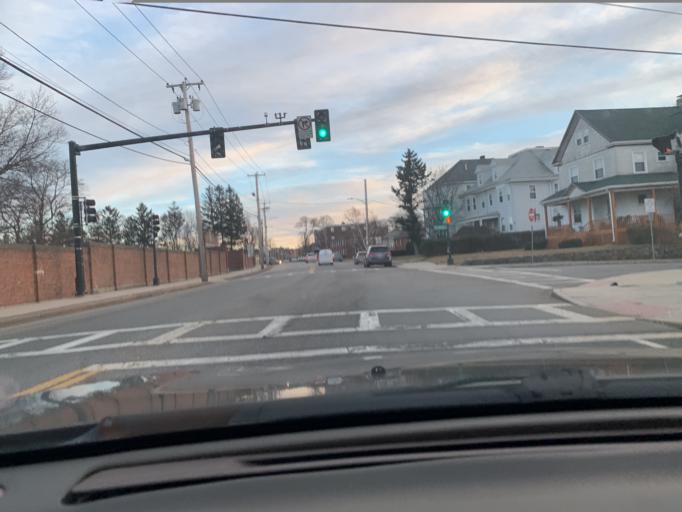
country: US
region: Massachusetts
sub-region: Norfolk County
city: Quincy
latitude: 42.2615
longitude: -71.0114
